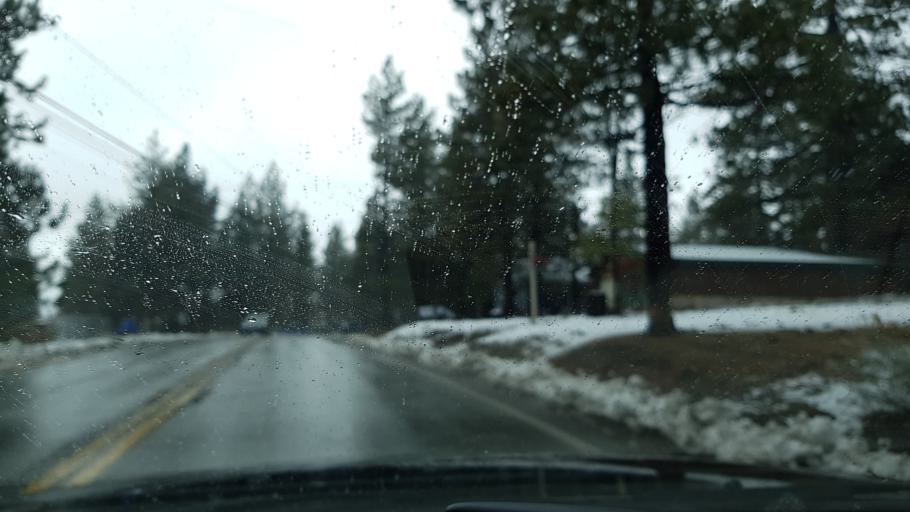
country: US
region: California
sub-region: San Bernardino County
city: Big Bear Lake
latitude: 34.2624
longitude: -116.9273
